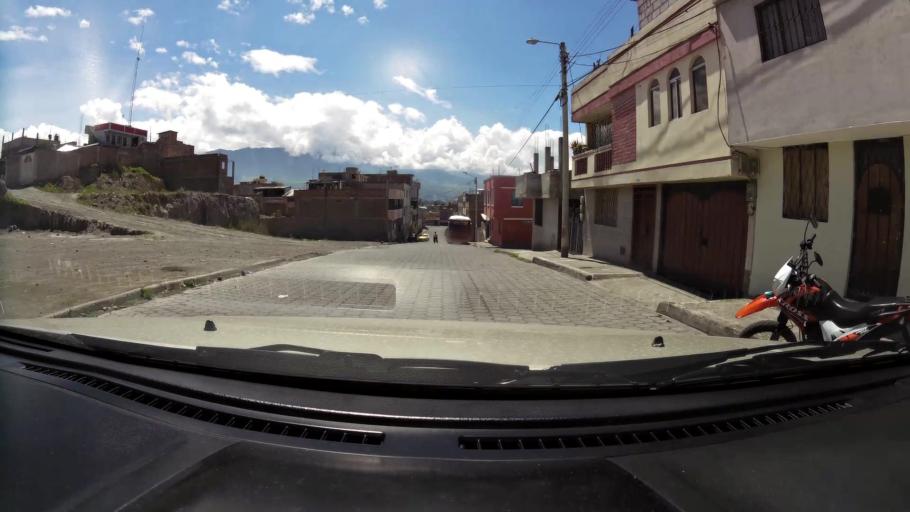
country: EC
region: Chimborazo
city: Riobamba
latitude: -1.6650
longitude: -78.6437
